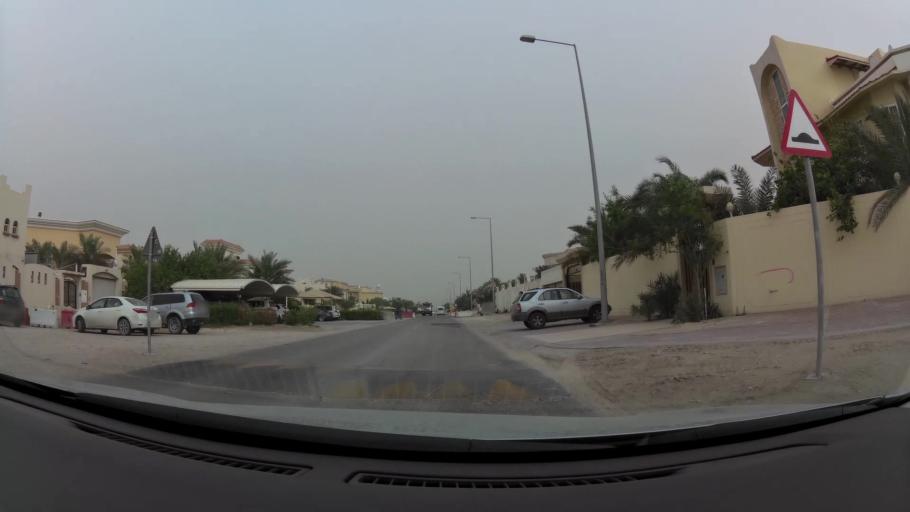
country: QA
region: Baladiyat ad Dawhah
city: Doha
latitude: 25.2513
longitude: 51.4954
